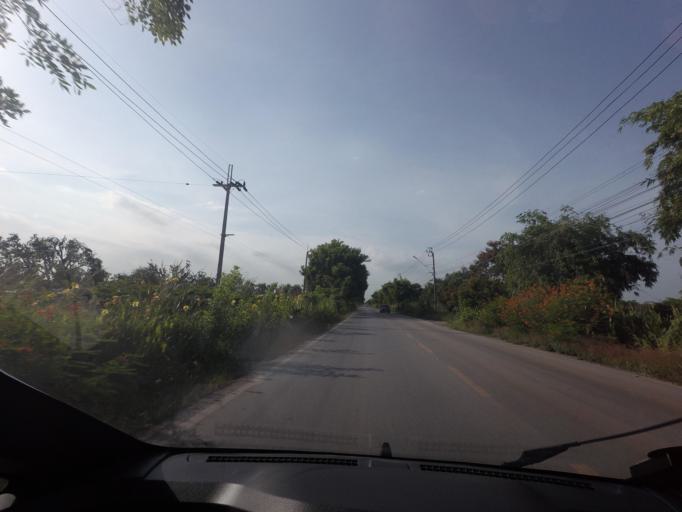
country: TH
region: Samut Prakan
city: Ban Khlong Bang Sao Thong
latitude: 13.7040
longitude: 100.8540
